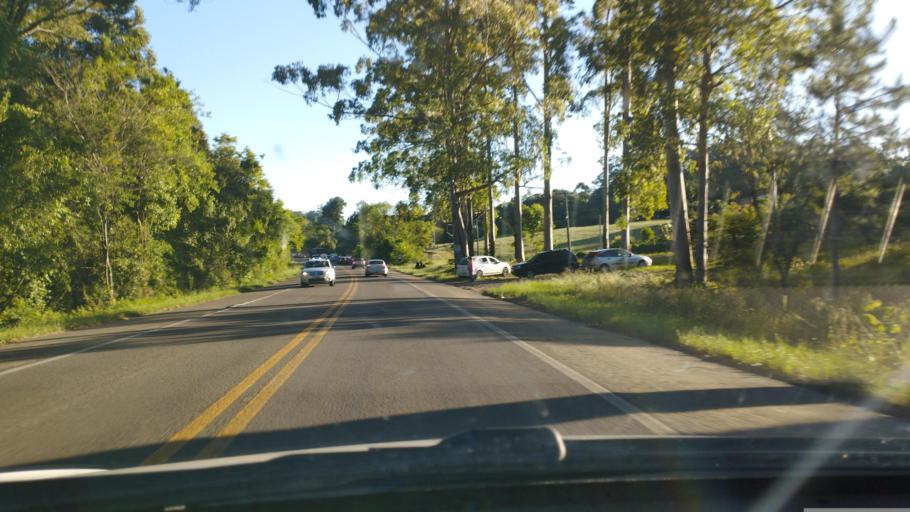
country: BR
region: Rio Grande do Sul
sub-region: Santa Maria
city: Santa Maria
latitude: -29.5971
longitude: -53.7673
